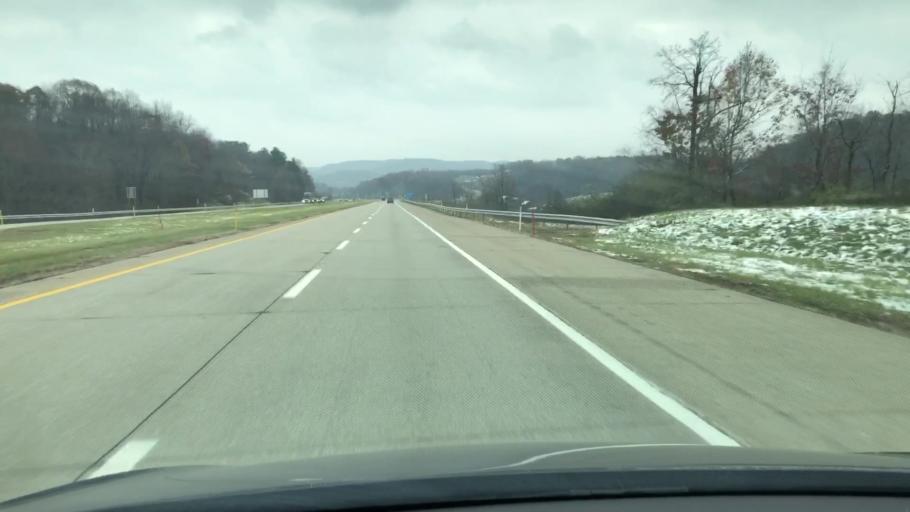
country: US
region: Pennsylvania
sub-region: Westmoreland County
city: New Stanton
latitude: 40.2453
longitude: -79.6086
